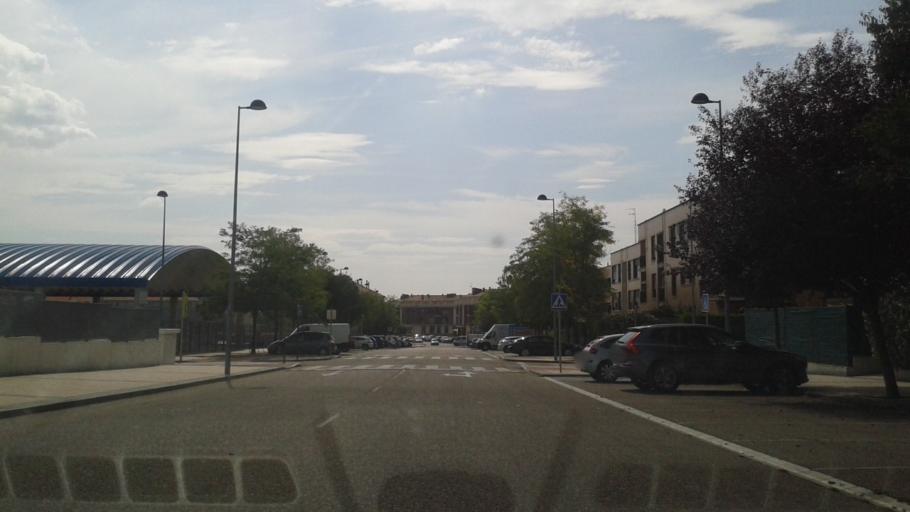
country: ES
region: Castille and Leon
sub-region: Provincia de Valladolid
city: Arroyo
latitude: 41.6275
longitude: -4.7769
